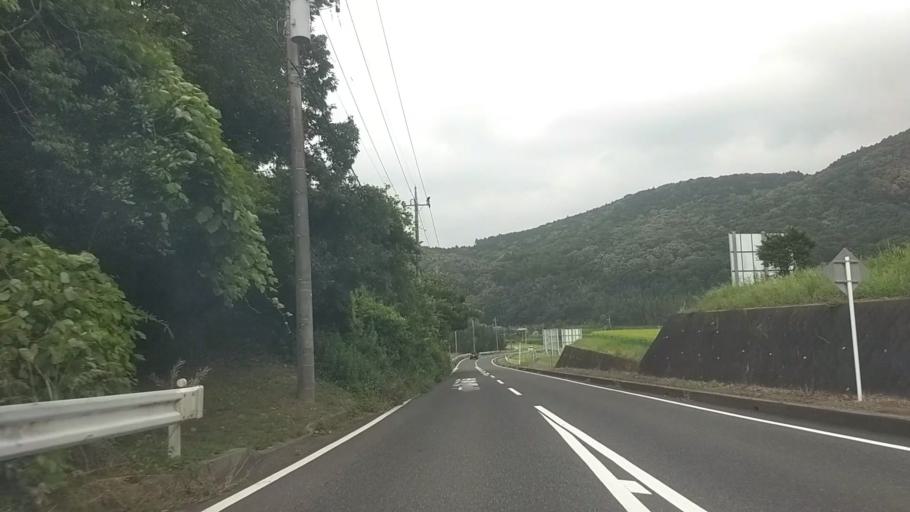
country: JP
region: Chiba
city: Kimitsu
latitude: 35.2596
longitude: 140.0030
